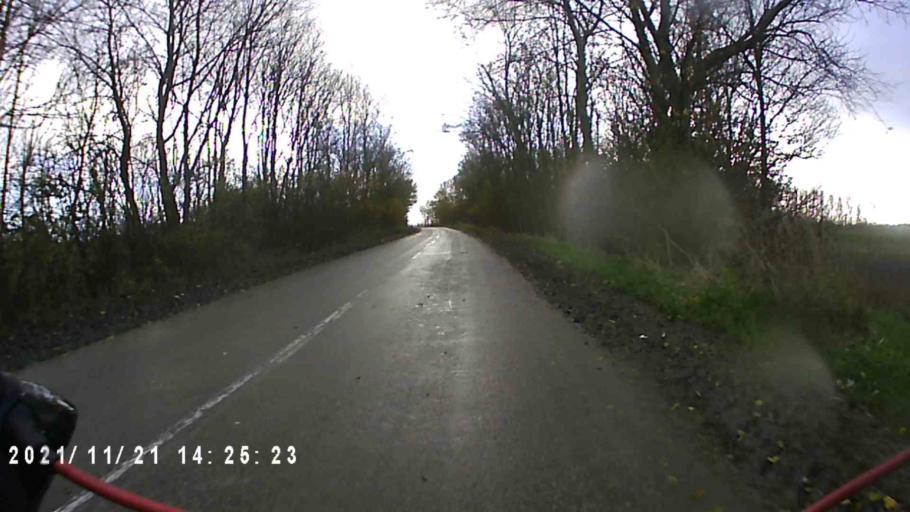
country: NL
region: Groningen
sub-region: Gemeente De Marne
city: Ulrum
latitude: 53.3675
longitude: 6.2937
